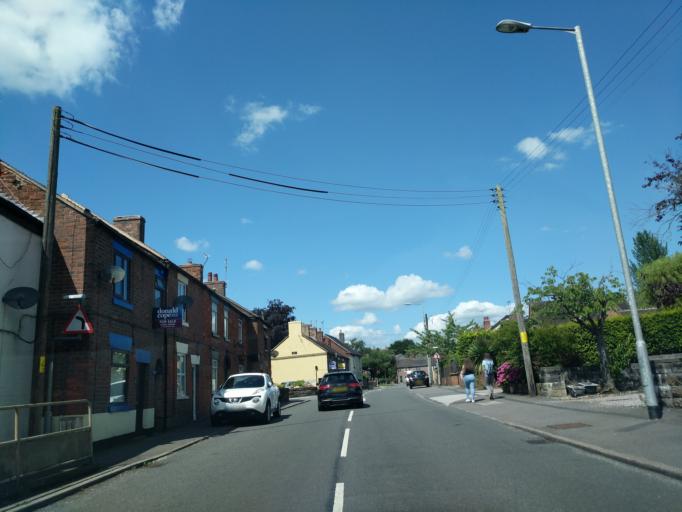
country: GB
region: England
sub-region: Staffordshire
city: Cheadle
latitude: 52.9521
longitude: -1.9850
